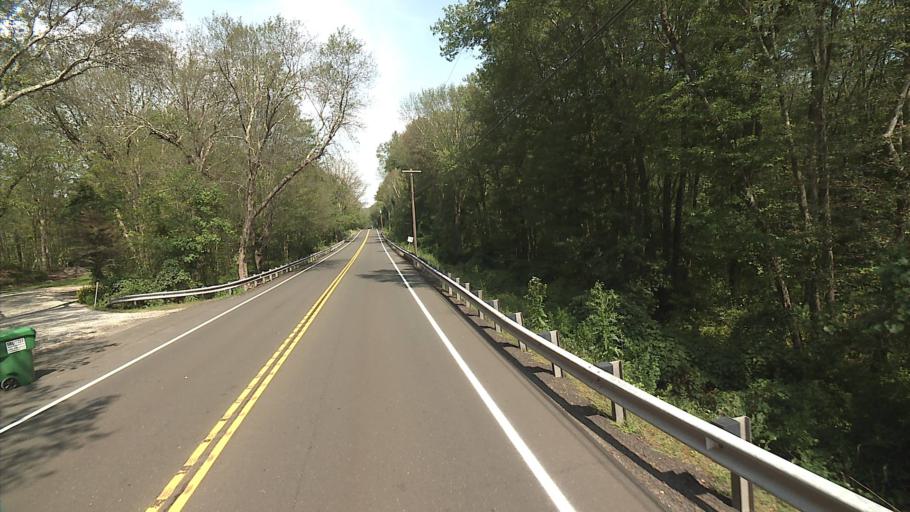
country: US
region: Connecticut
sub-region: Middlesex County
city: Durham
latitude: 41.4304
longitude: -72.6497
